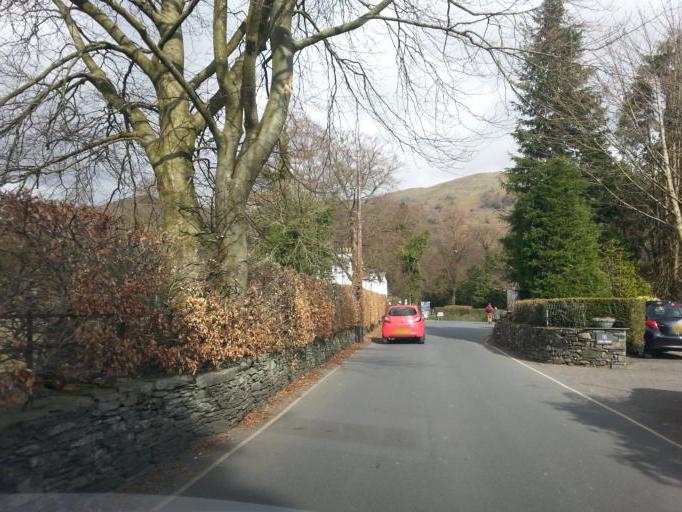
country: GB
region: England
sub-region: Cumbria
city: Ambleside
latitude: 54.4572
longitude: -3.0271
